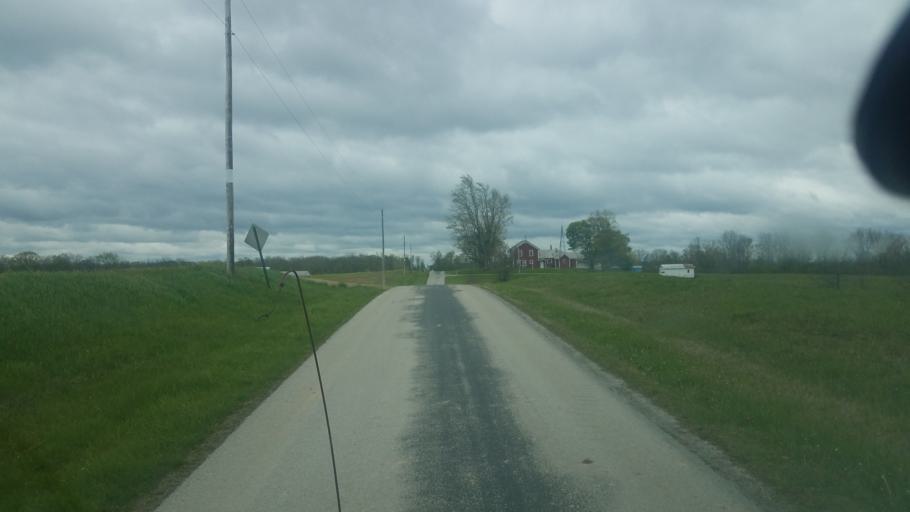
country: US
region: Ohio
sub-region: Wyandot County
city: Upper Sandusky
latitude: 40.7664
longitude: -83.1450
